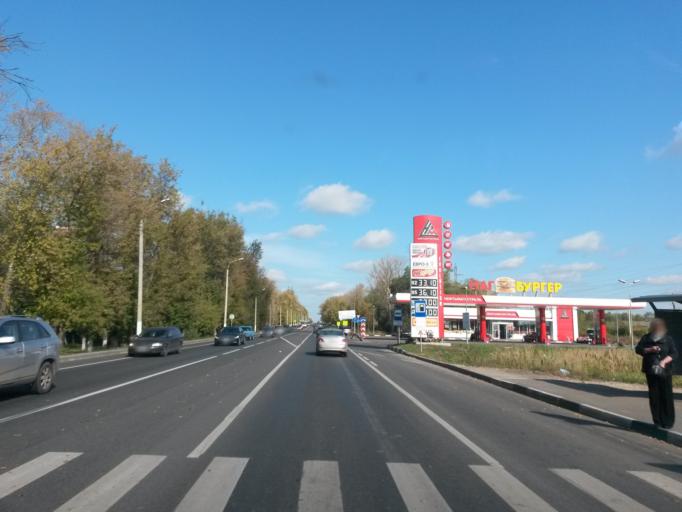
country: RU
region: Moskovskaya
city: L'vovskiy
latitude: 55.3157
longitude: 37.5287
